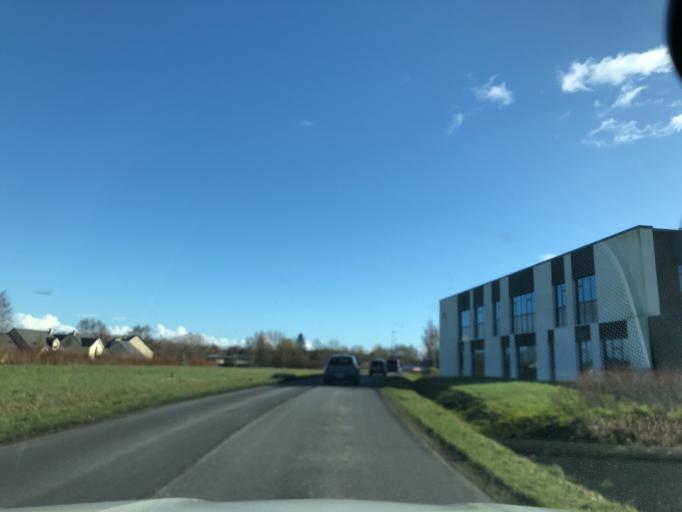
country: FR
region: Lower Normandy
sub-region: Departement du Calvados
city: Epron
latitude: 49.2196
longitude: -0.3567
